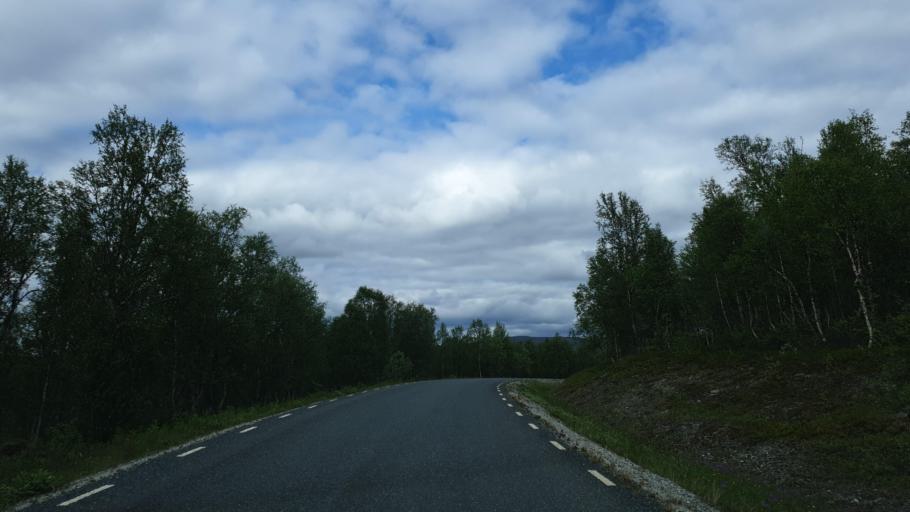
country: NO
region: Nordland
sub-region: Hattfjelldal
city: Hattfjelldal
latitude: 65.4227
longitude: 14.8824
